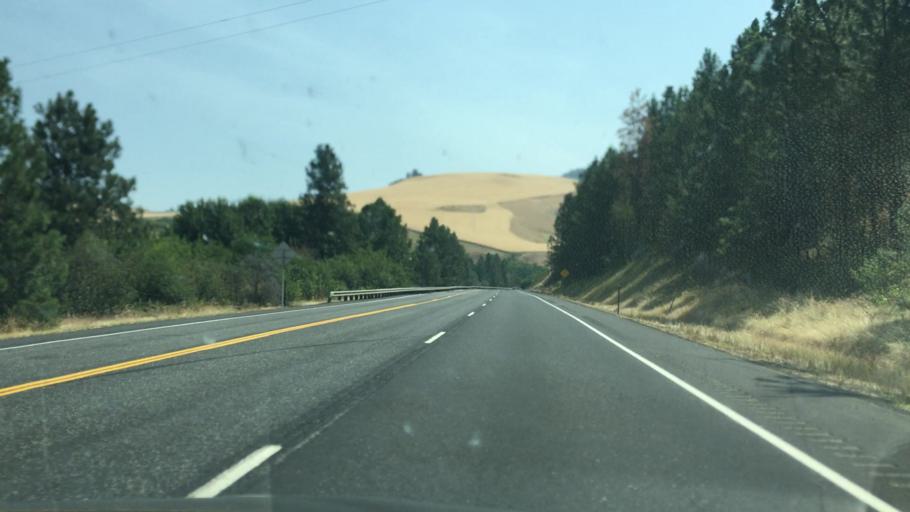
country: US
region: Idaho
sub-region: Nez Perce County
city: Lapwai
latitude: 46.3725
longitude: -116.6615
